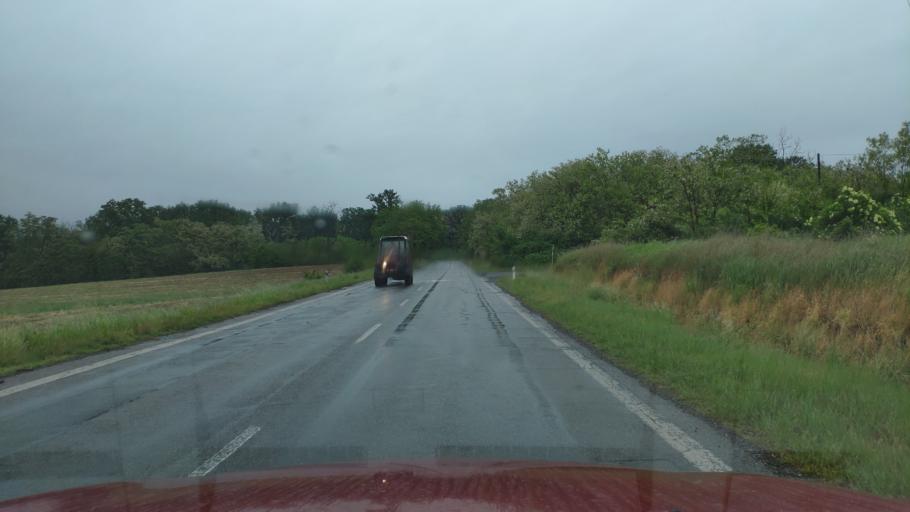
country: HU
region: Borsod-Abauj-Zemplen
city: Ricse
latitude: 48.4363
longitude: 21.9327
